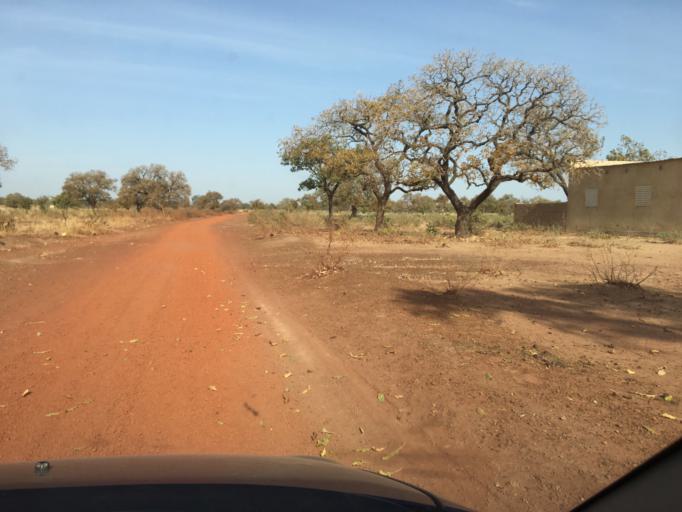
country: BF
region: Plateau-Central
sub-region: Province du Kourweogo
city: Bousse
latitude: 12.5653
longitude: -1.9088
